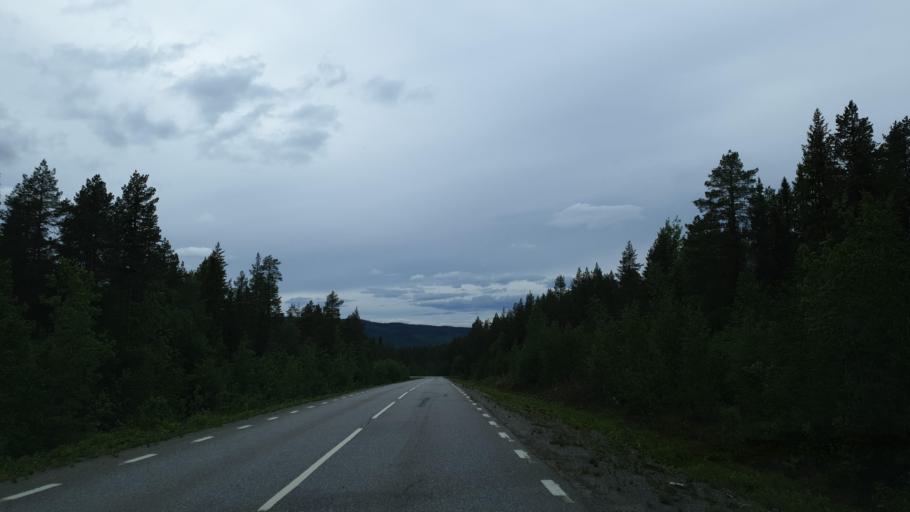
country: SE
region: Vaesterbotten
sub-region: Sorsele Kommun
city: Sorsele
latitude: 65.5437
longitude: 17.4578
